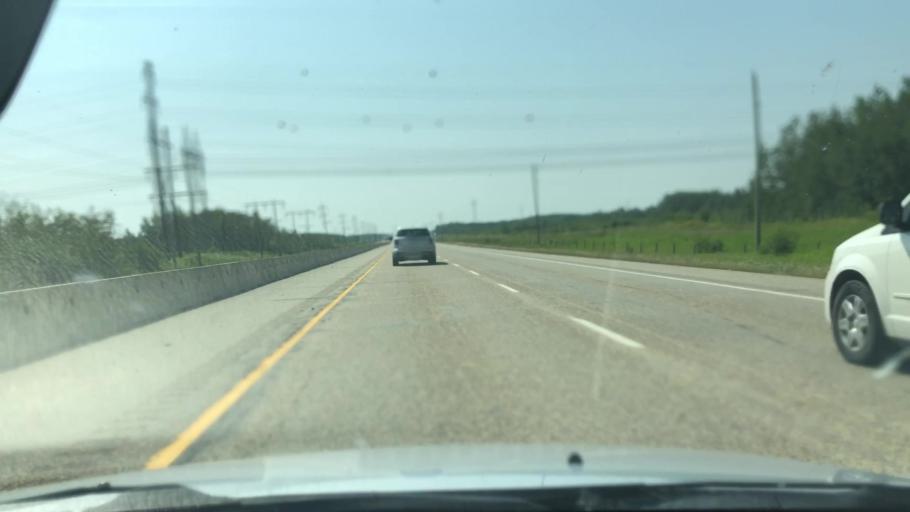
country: CA
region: Alberta
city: Devon
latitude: 53.4630
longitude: -113.7626
